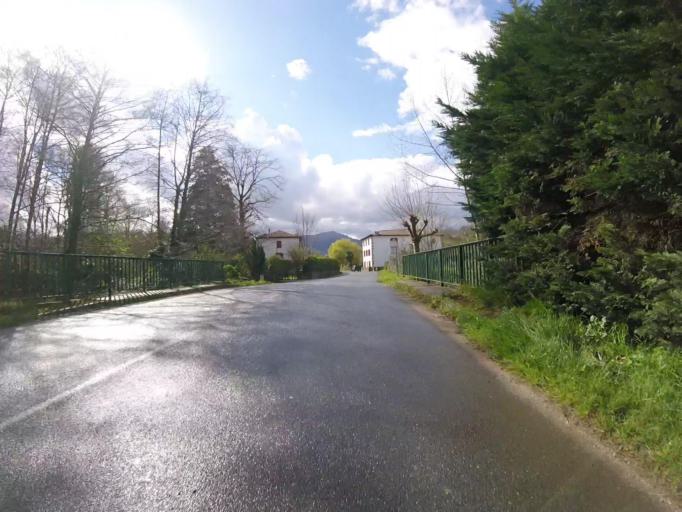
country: FR
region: Aquitaine
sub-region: Departement des Pyrenees-Atlantiques
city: Sare
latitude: 43.3080
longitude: -1.5727
